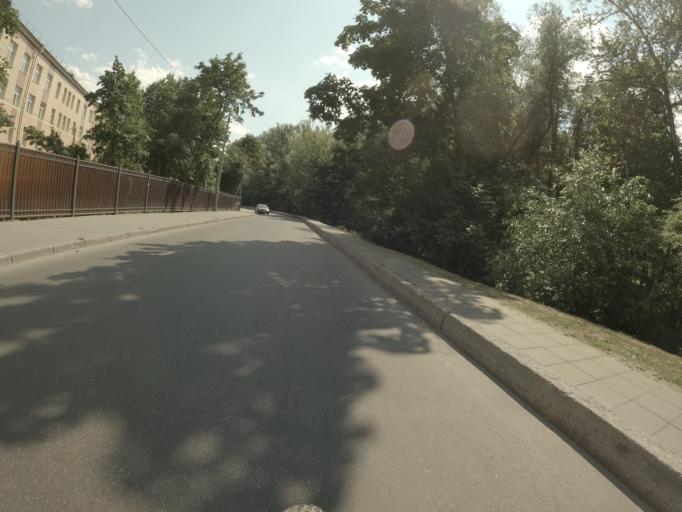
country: RU
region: St.-Petersburg
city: Admiralteisky
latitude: 59.9048
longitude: 30.2666
